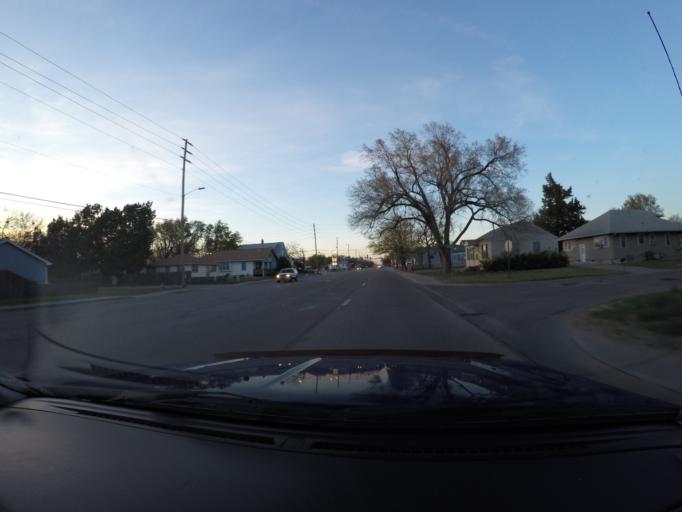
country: US
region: Kansas
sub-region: Saline County
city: Salina
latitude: 38.8391
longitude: -97.5940
